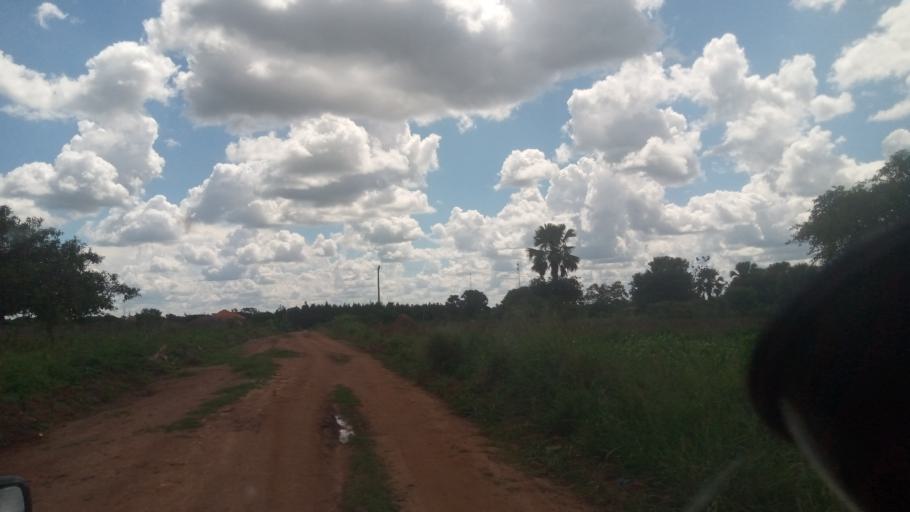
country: UG
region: Northern Region
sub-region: Lira District
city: Lira
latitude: 2.2319
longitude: 32.9050
